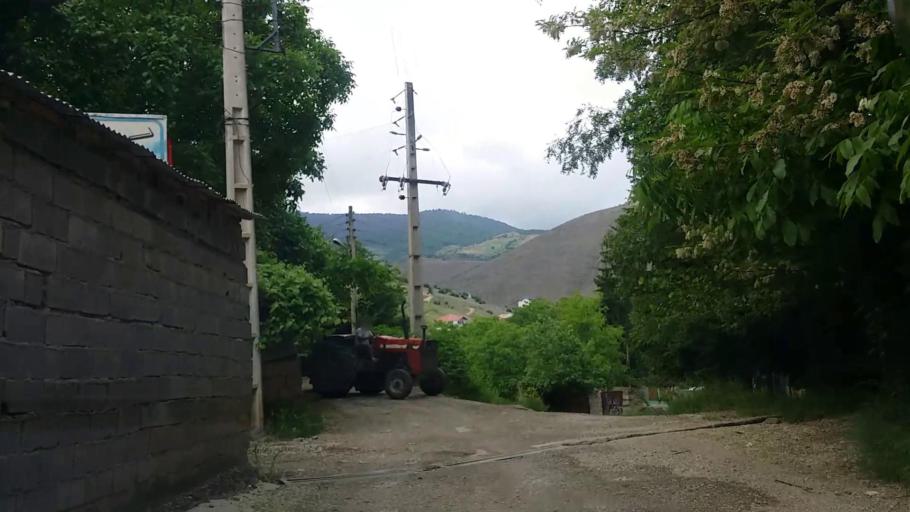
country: IR
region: Mazandaran
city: `Abbasabad
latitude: 36.4976
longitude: 51.1446
